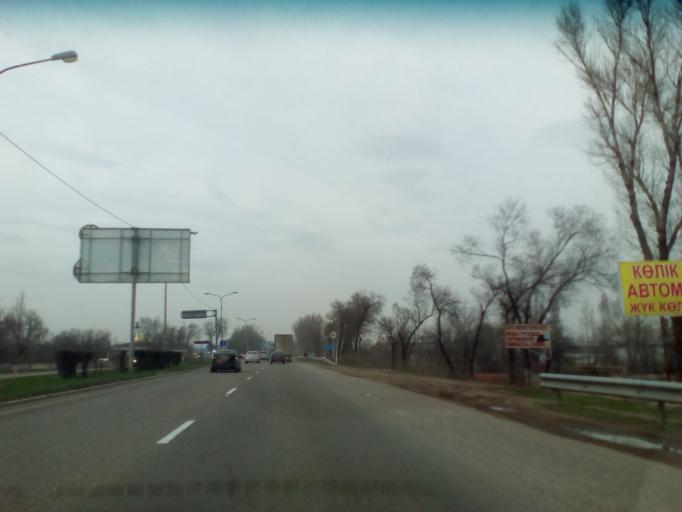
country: KZ
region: Almaty Oblysy
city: Burunday
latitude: 43.2190
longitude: 76.6424
